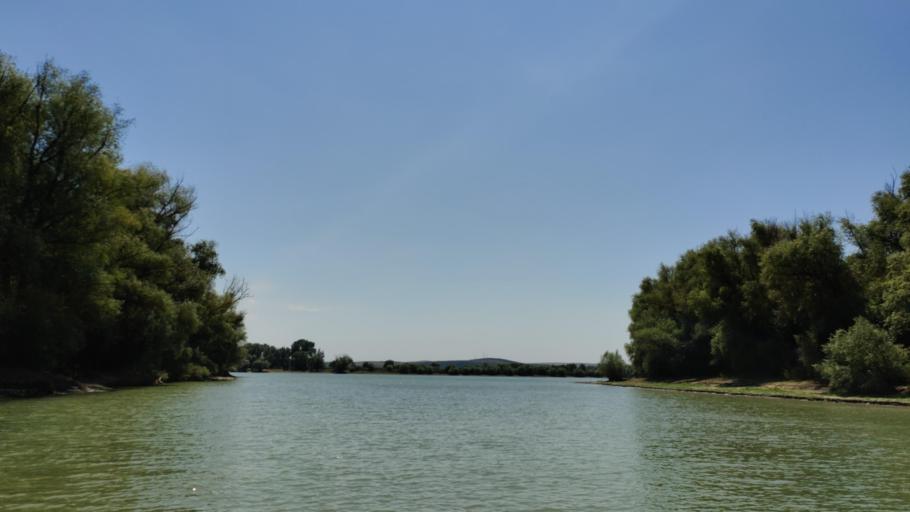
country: RO
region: Tulcea
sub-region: Municipiul Tulcea
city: Tulcea
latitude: 45.2058
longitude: 28.8530
